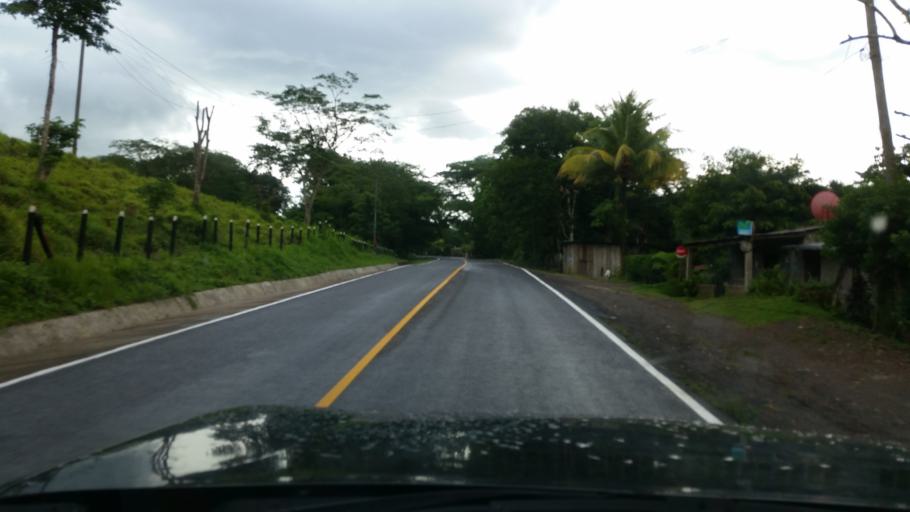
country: NI
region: Matagalpa
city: San Ramon
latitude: 13.0517
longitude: -85.7607
